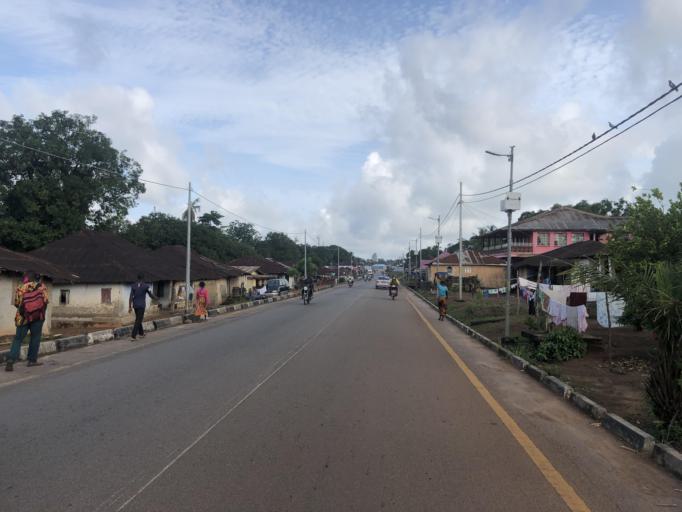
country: SL
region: Northern Province
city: Magburaka
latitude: 8.7209
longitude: -11.9413
